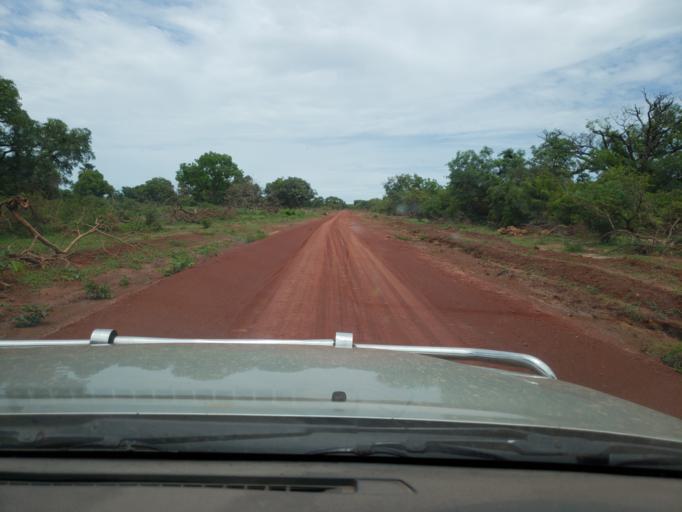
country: ML
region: Sikasso
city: Sikasso
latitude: 11.6558
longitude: -6.3419
